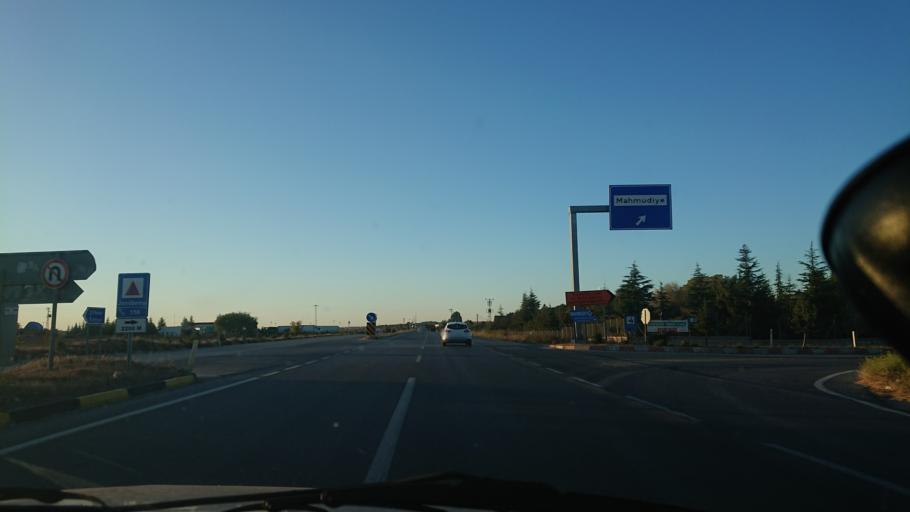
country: TR
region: Eskisehir
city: Mahmudiye
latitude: 39.4752
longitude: 30.9922
